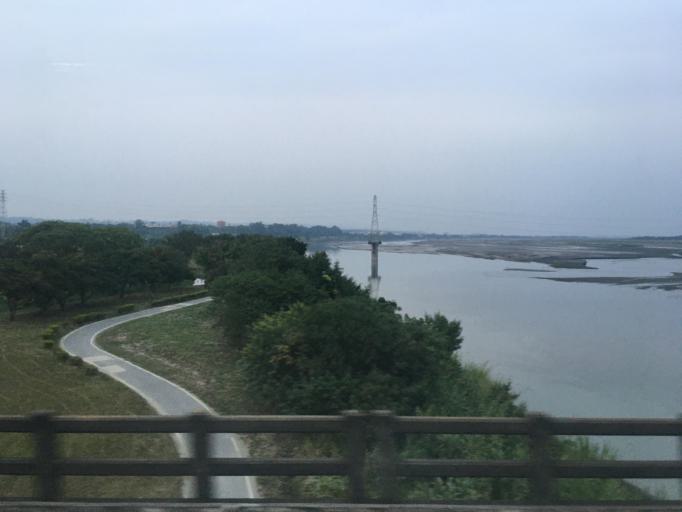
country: TW
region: Taiwan
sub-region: Pingtung
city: Pingtung
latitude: 22.6624
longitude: 120.4305
